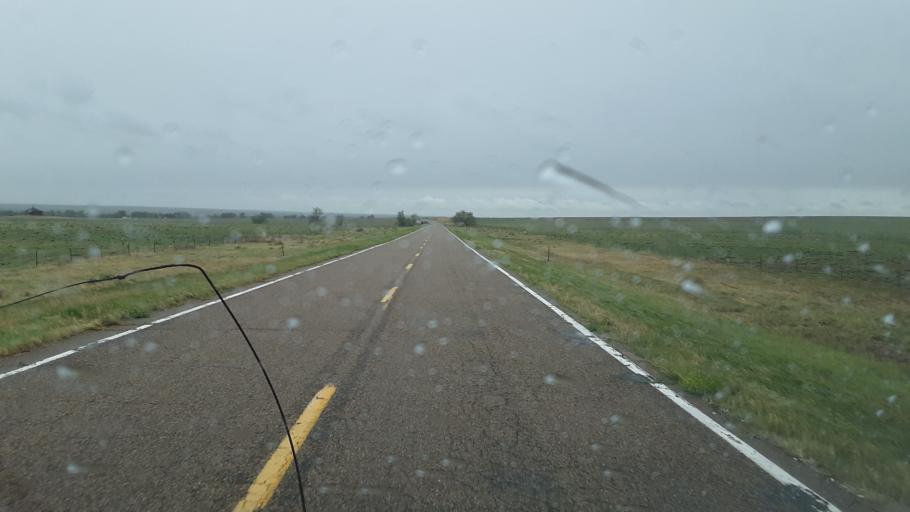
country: US
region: Colorado
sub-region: Lincoln County
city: Hugo
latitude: 38.8640
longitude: -103.1345
